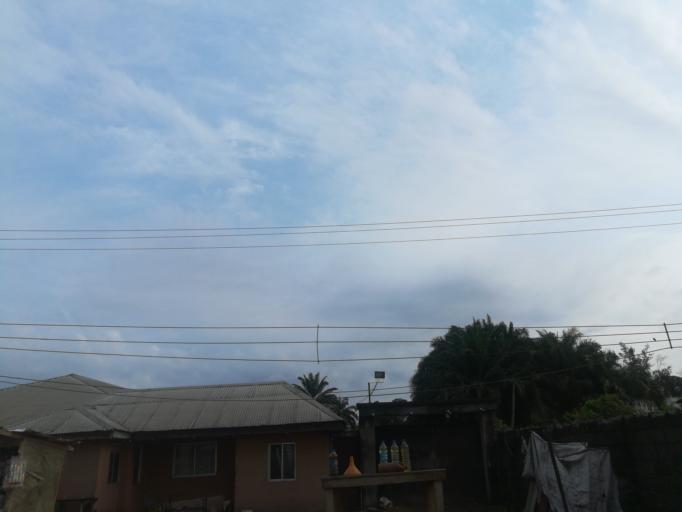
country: NG
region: Rivers
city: Okrika
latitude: 4.7651
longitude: 7.0850
